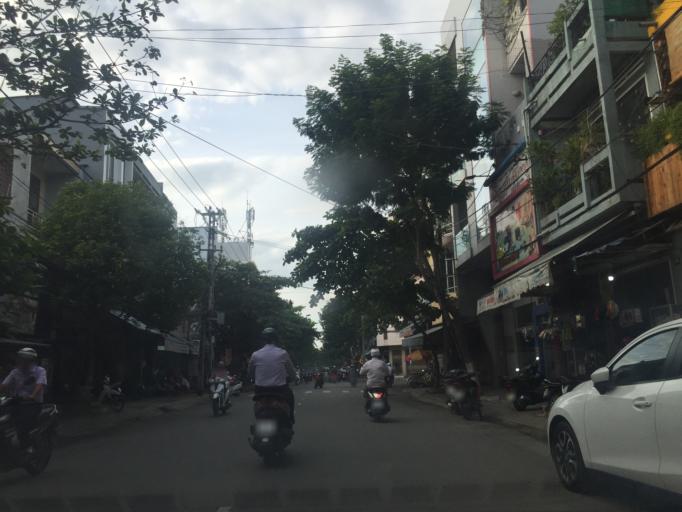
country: VN
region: Da Nang
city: Da Nang
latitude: 16.0767
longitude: 108.2122
